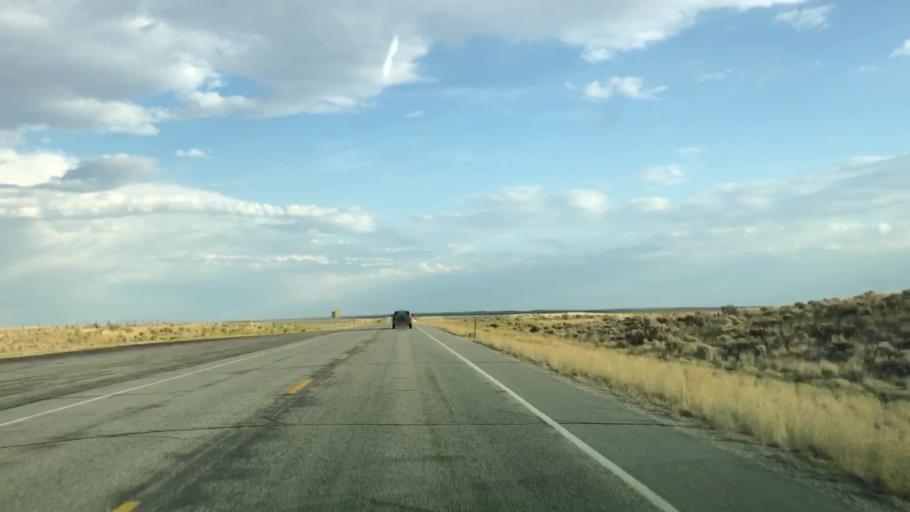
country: US
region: Wyoming
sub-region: Sublette County
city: Marbleton
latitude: 42.3274
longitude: -109.5135
